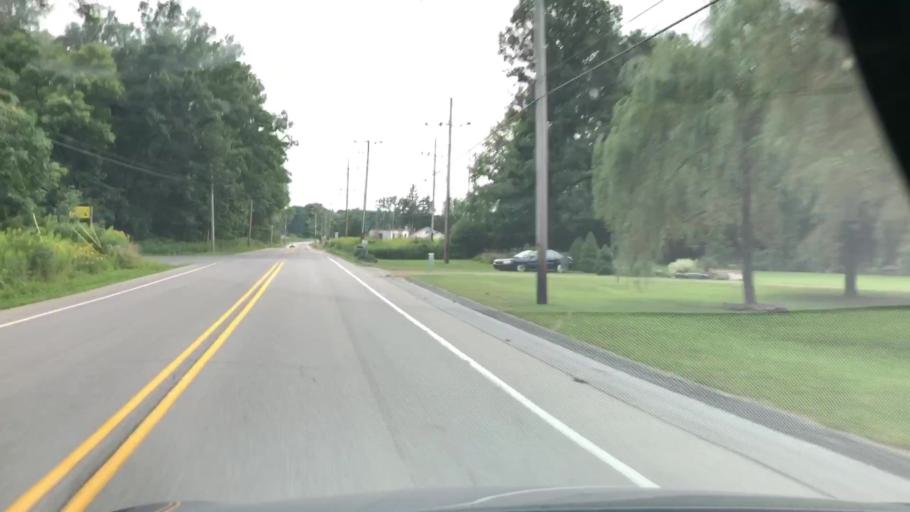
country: US
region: Pennsylvania
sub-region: Crawford County
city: Titusville
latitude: 41.5485
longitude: -79.7019
